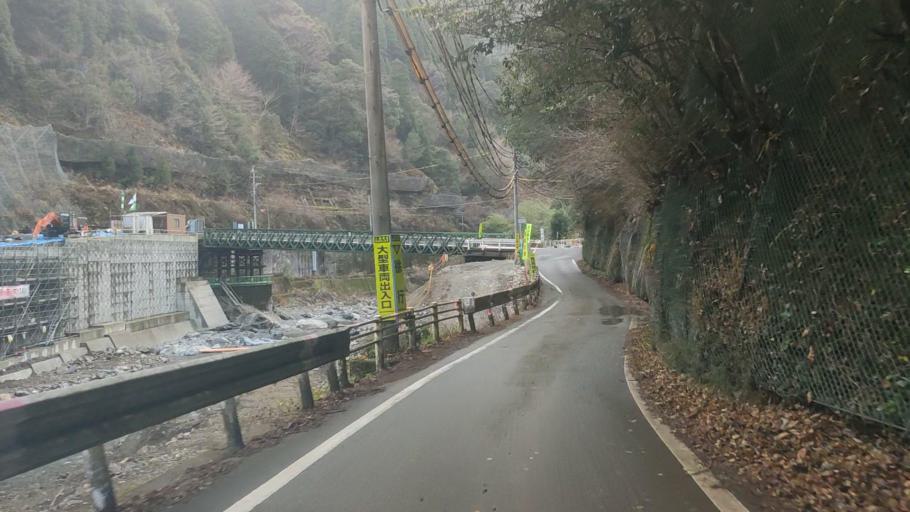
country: JP
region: Kumamoto
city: Matsubase
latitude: 32.4812
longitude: 130.8889
